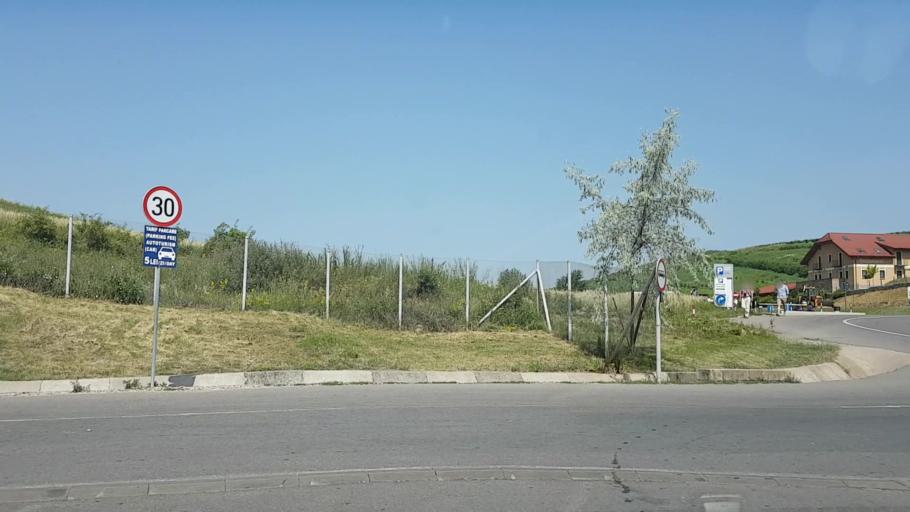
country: RO
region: Cluj
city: Turda
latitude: 46.5890
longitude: 23.7876
